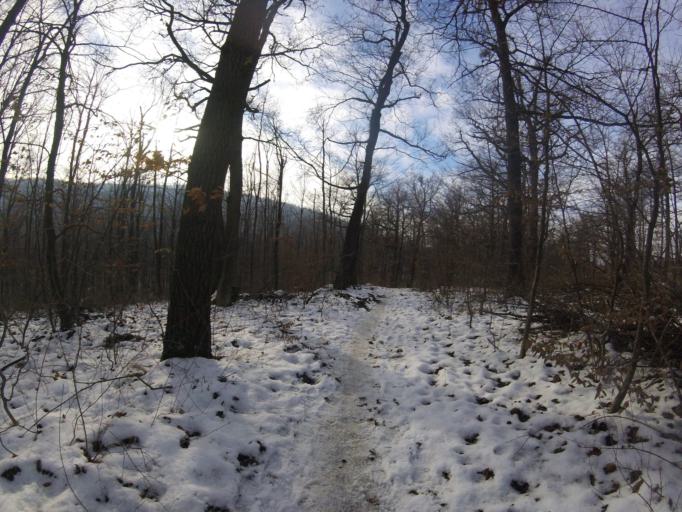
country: HU
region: Pest
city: Dunabogdany
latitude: 47.7388
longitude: 19.0166
